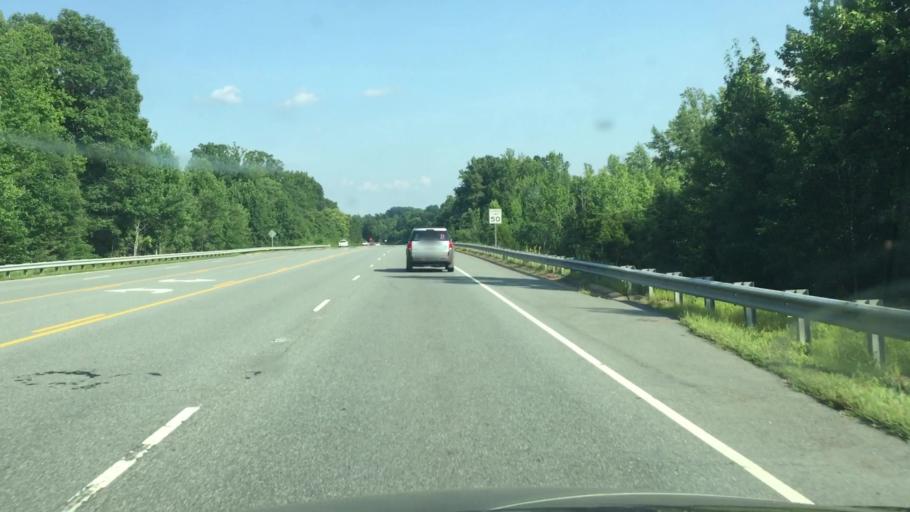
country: US
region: North Carolina
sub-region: Rockingham County
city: Reidsville
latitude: 36.3682
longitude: -79.6442
